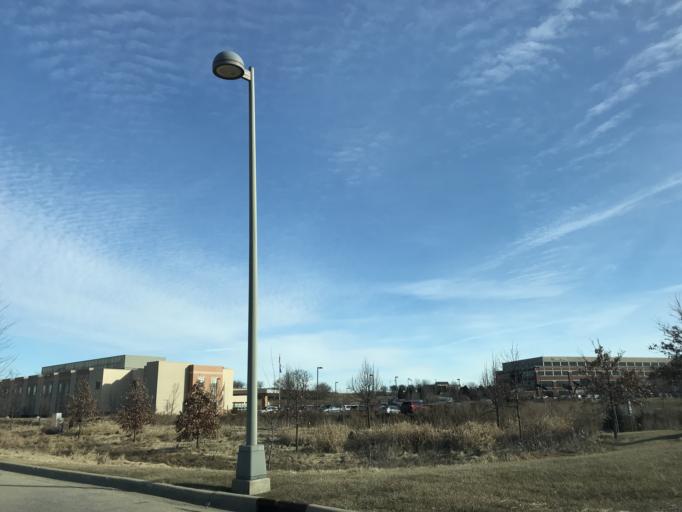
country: US
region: Wisconsin
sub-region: Dane County
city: Windsor
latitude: 43.1529
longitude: -89.2993
